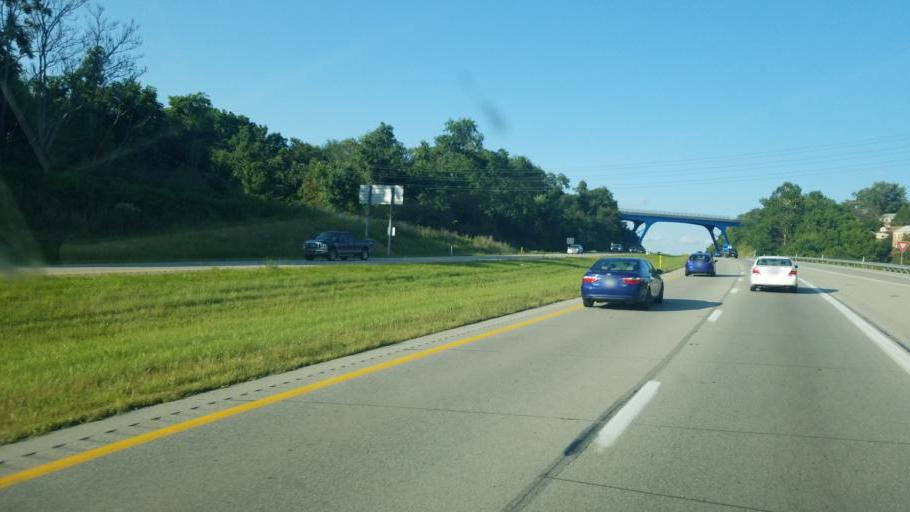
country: US
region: Pennsylvania
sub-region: Washington County
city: Houston
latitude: 40.2468
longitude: -80.1971
